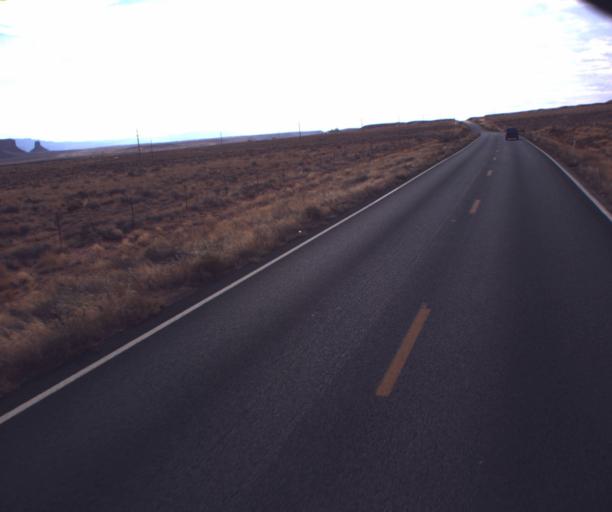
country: US
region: Arizona
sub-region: Apache County
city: Many Farms
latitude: 36.6129
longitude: -109.5783
